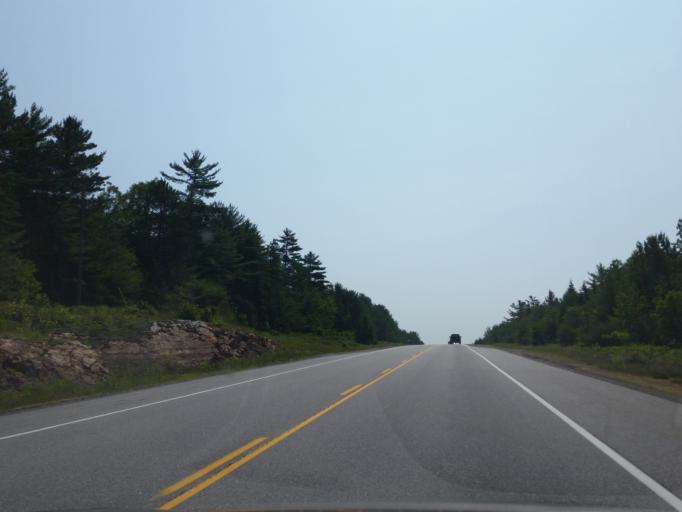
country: CA
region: Ontario
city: Mattawa
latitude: 46.3003
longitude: -78.5599
